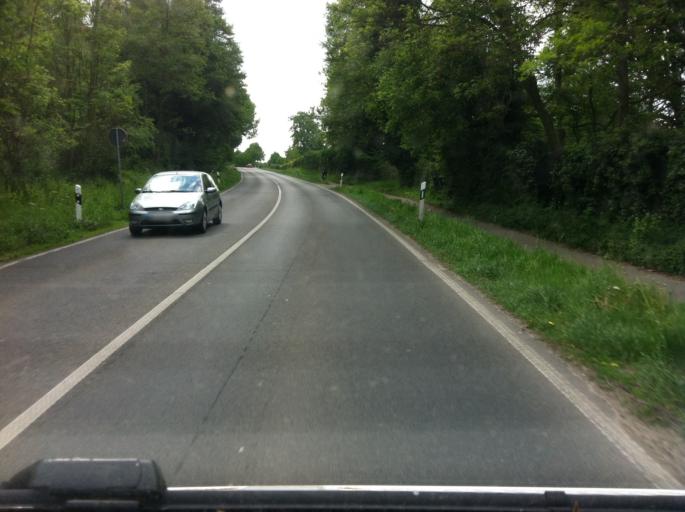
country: DE
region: North Rhine-Westphalia
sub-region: Regierungsbezirk Dusseldorf
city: Bruggen
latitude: 51.2332
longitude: 6.1922
